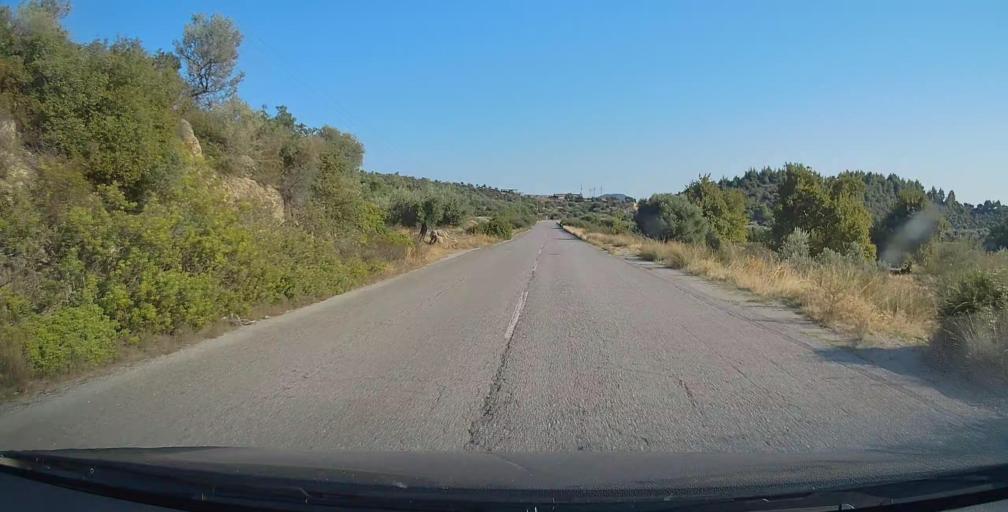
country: GR
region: Central Macedonia
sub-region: Nomos Chalkidikis
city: Sykia
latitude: 40.0040
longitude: 23.8863
